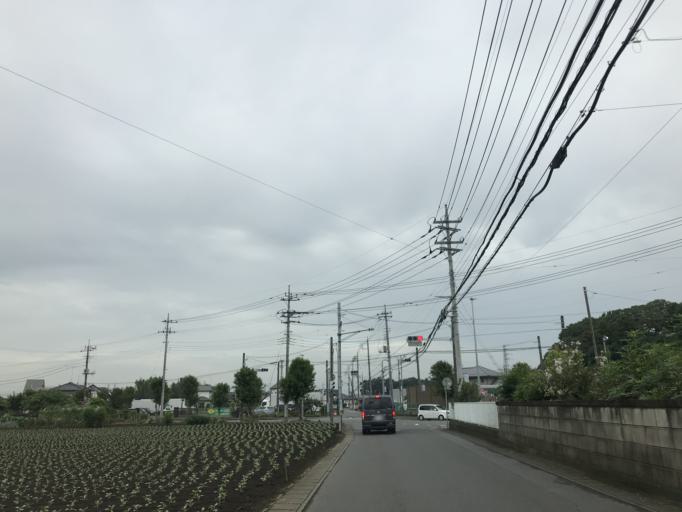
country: JP
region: Ibaraki
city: Koga
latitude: 36.1572
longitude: 139.7732
